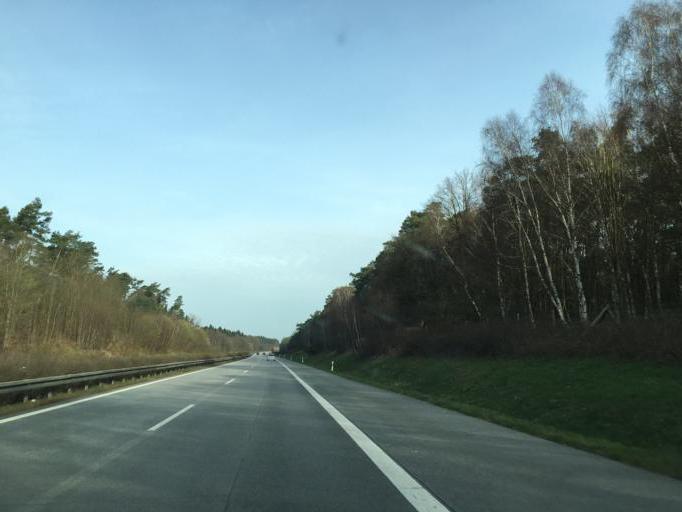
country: DE
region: Mecklenburg-Vorpommern
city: Malchow
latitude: 53.4148
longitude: 12.4360
